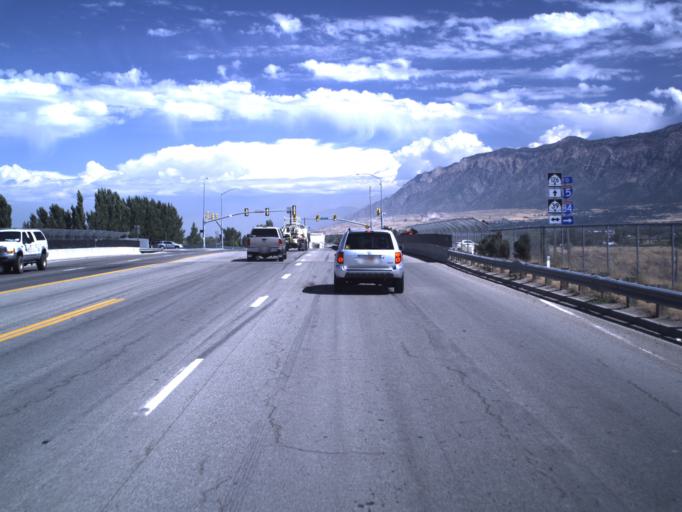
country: US
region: Utah
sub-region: Weber County
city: Marriott-Slaterville
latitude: 41.2434
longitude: -112.0253
